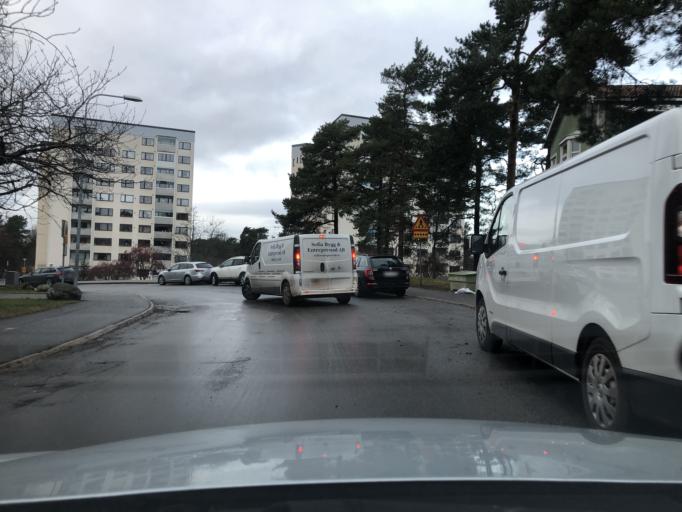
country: SE
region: Stockholm
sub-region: Stockholms Kommun
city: Arsta
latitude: 59.3012
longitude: 18.0540
